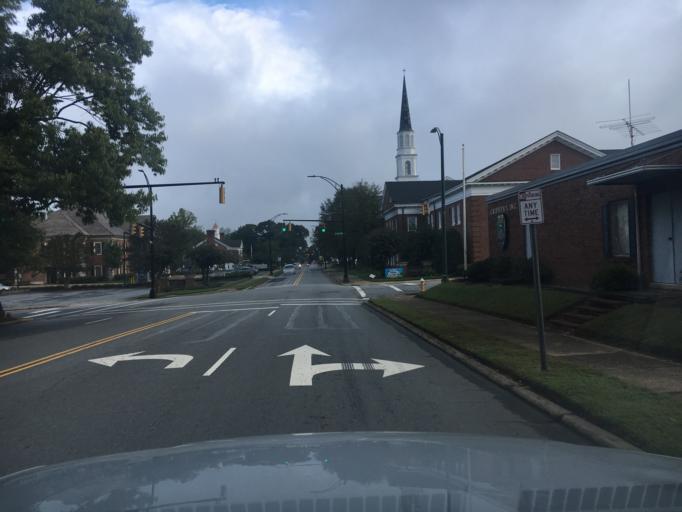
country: US
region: North Carolina
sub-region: Catawba County
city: Hickory
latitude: 35.7327
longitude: -81.3445
